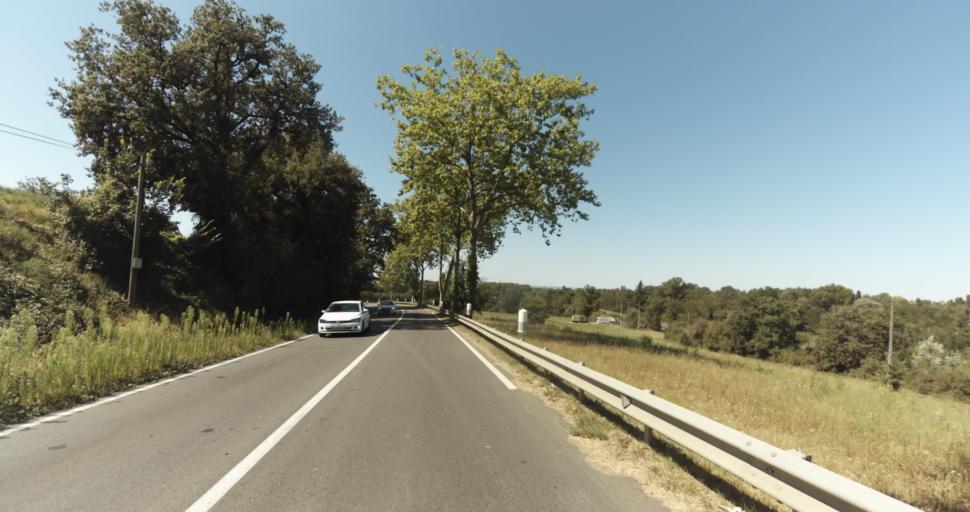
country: FR
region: Midi-Pyrenees
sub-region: Departement de la Haute-Garonne
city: Montrabe
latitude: 43.6446
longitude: 1.5072
